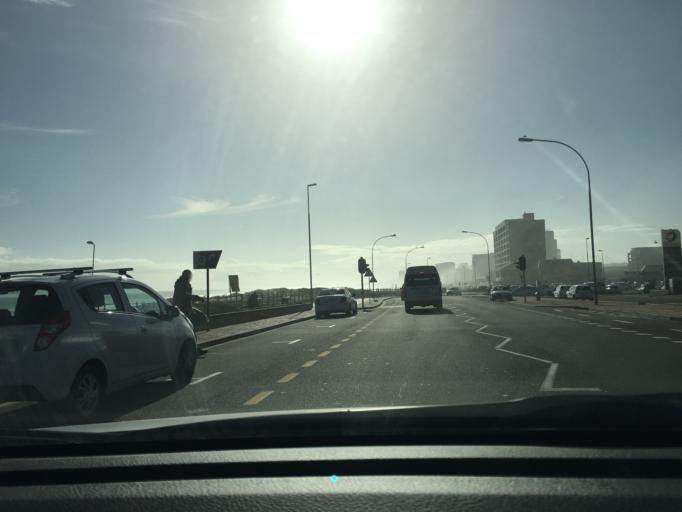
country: ZA
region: Western Cape
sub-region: City of Cape Town
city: Sunset Beach
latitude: -33.8227
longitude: 18.4772
